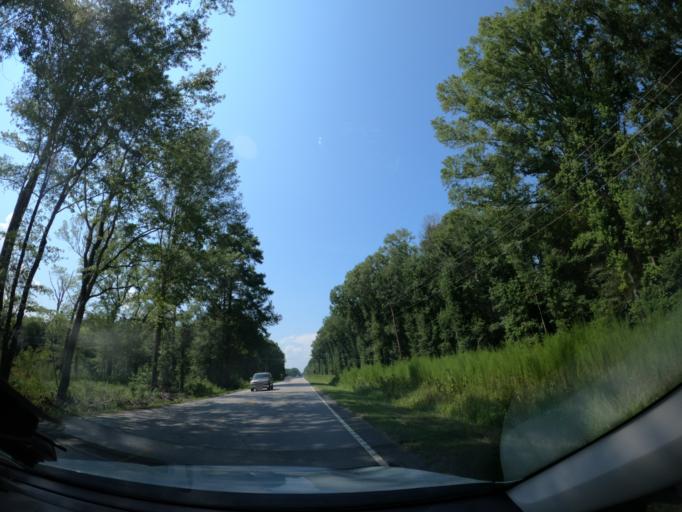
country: US
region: South Carolina
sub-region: Richland County
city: Hopkins
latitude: 33.8835
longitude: -80.9066
